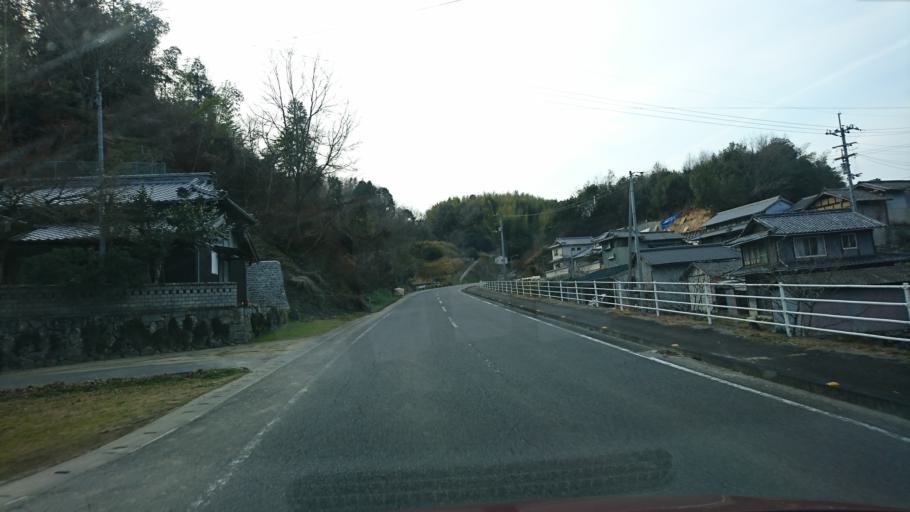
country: JP
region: Ehime
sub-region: Shikoku-chuo Shi
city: Matsuyama
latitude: 33.9017
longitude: 132.8152
